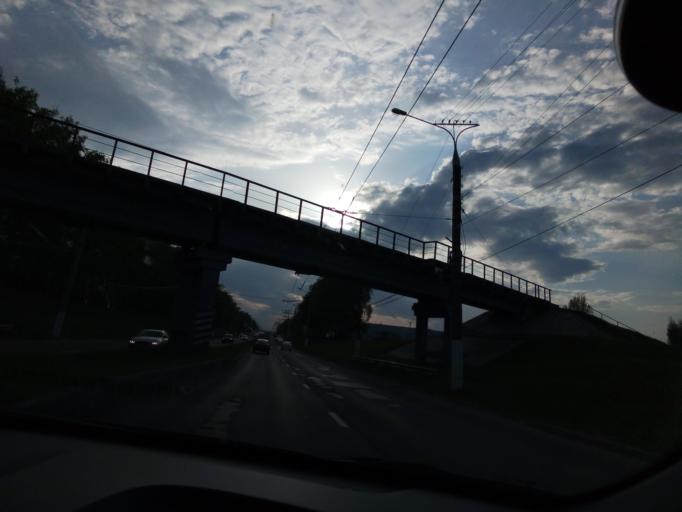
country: RU
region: Chuvashia
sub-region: Cheboksarskiy Rayon
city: Cheboksary
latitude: 56.1273
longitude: 47.3297
